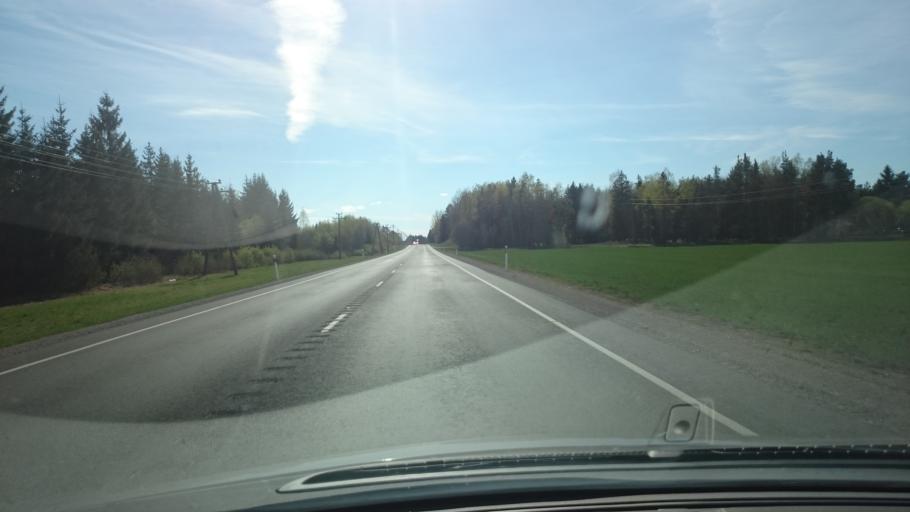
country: EE
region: Laeaene-Virumaa
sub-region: Rakvere linn
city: Rakvere
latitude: 59.3510
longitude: 26.3023
